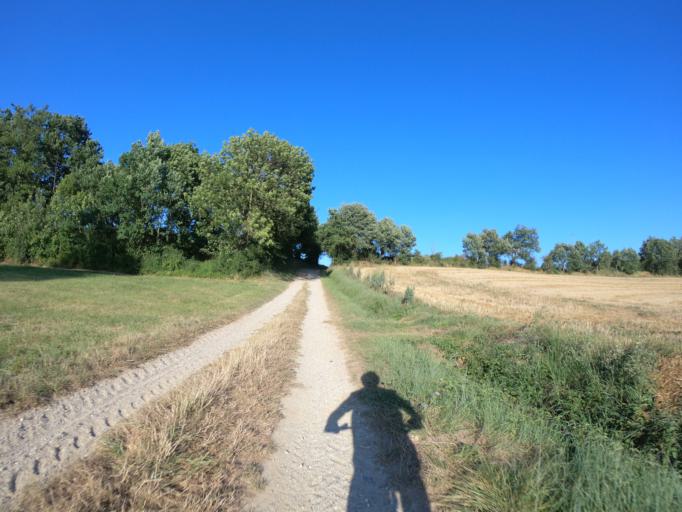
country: FR
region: Midi-Pyrenees
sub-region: Departement de l'Ariege
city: La Tour-du-Crieu
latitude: 43.0954
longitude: 1.7243
